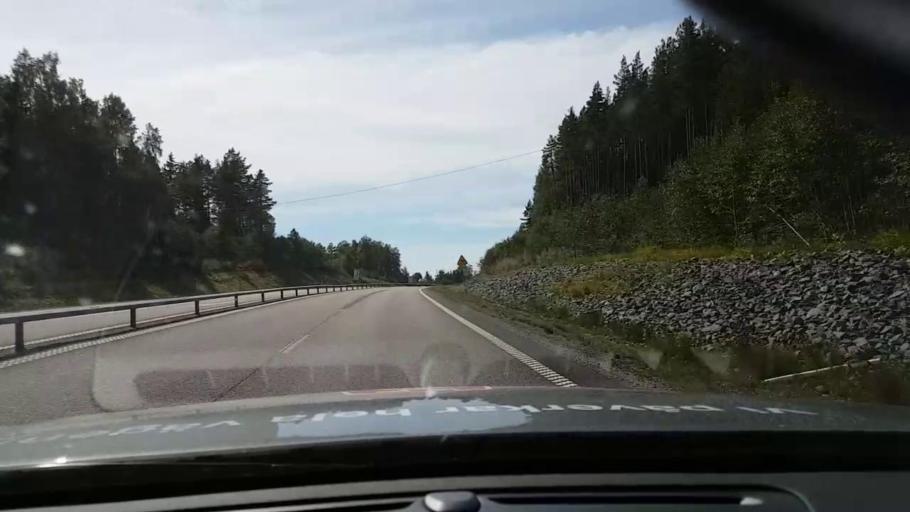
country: SE
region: Vaesternorrland
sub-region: OErnskoeldsviks Kommun
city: Ornskoldsvik
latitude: 63.3087
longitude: 18.9282
